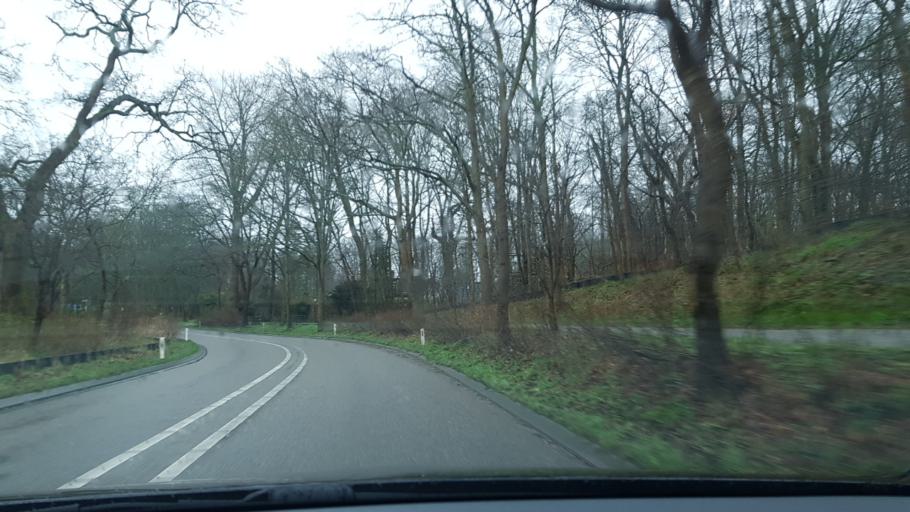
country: NL
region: North Holland
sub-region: Gemeente Bloemendaal
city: Bloemendaal
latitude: 52.3871
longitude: 4.5993
